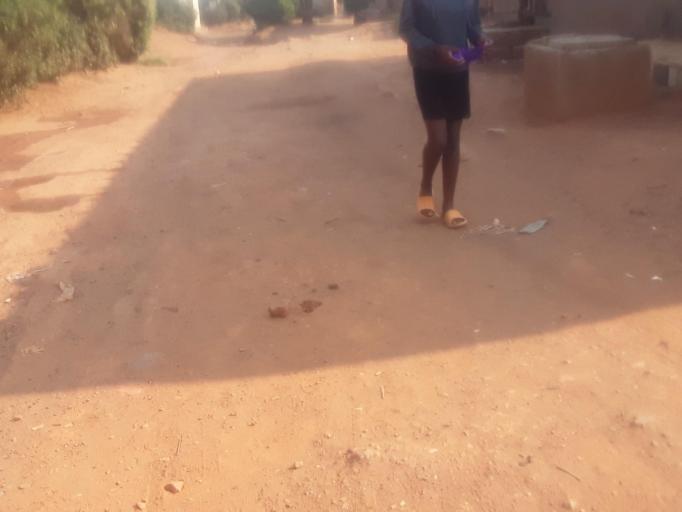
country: ZM
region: Lusaka
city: Lusaka
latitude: -15.3588
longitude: 28.2922
